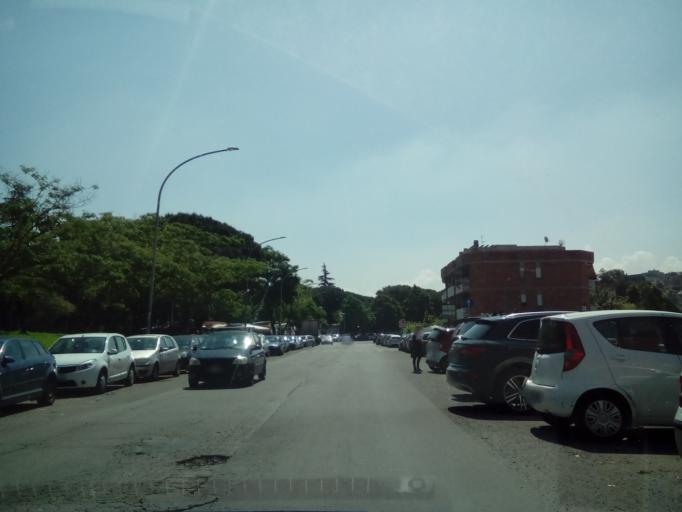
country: IT
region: Latium
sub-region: Citta metropolitana di Roma Capitale
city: Rome
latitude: 41.8860
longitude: 12.5873
